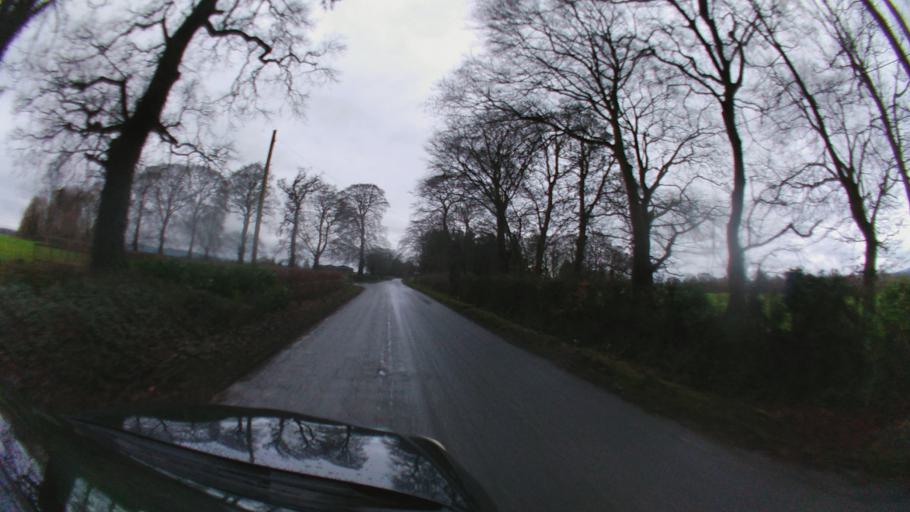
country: IE
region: Leinster
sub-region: County Carlow
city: Bagenalstown
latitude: 52.6627
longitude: -6.9909
